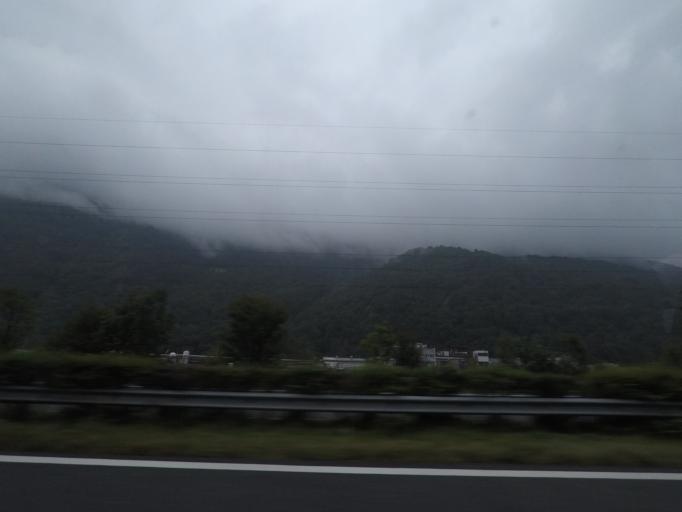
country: CH
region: Valais
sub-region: Martigny District
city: Evionnaz
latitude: 46.1724
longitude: 7.0265
